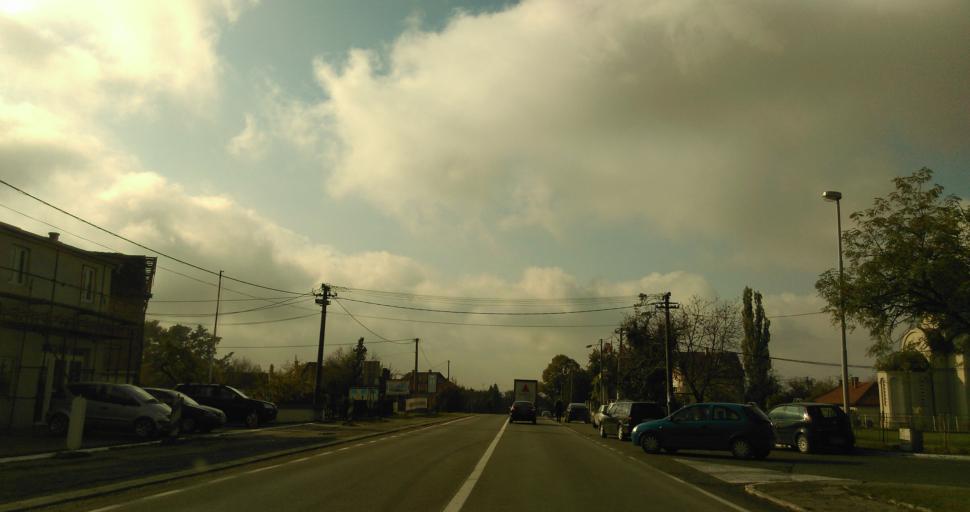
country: RS
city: Stepojevac
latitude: 44.5105
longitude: 20.2945
